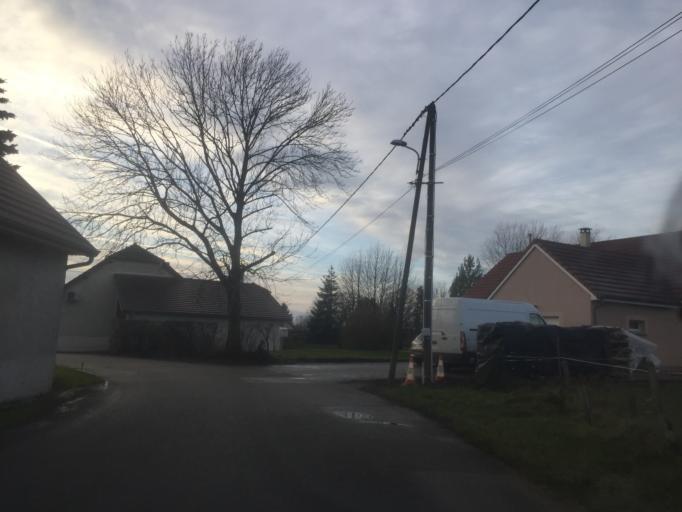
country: FR
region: Franche-Comte
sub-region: Departement du Jura
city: Orchamps
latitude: 47.1285
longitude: 5.6703
